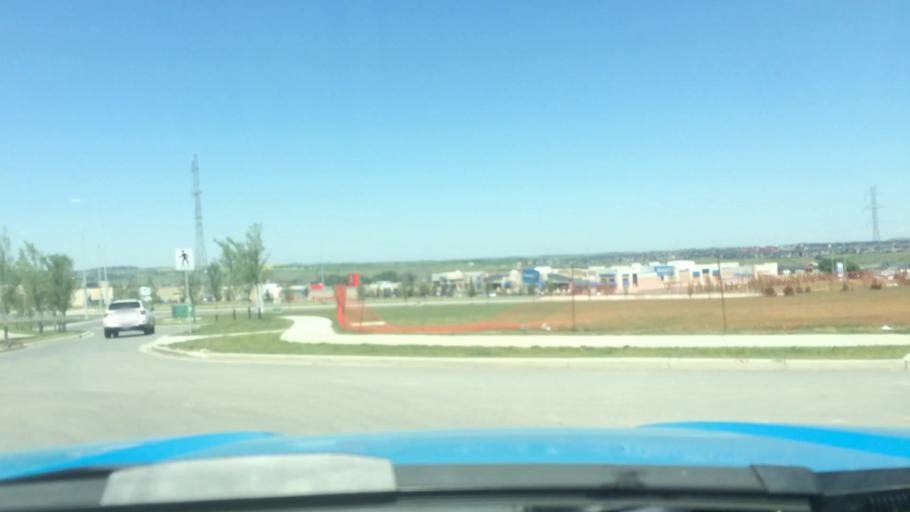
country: CA
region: Alberta
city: Calgary
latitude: 51.1666
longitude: -114.1469
